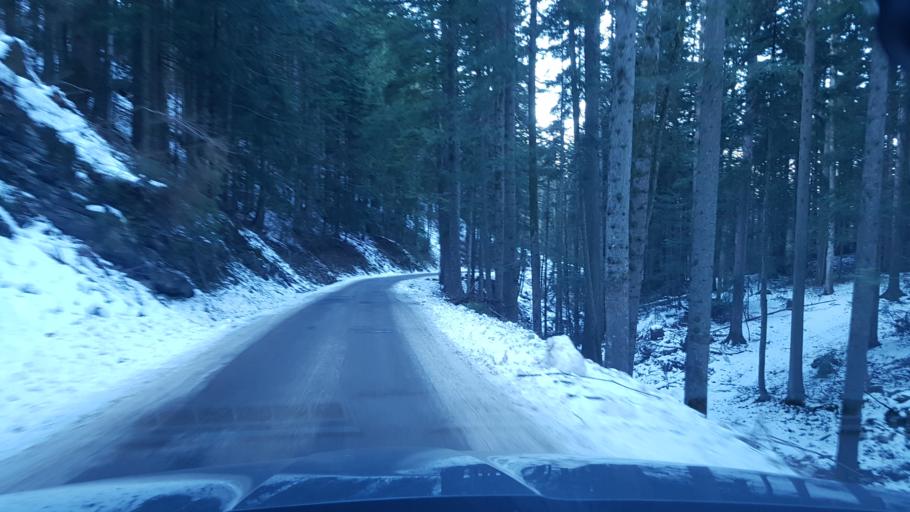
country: AT
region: Salzburg
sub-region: Politischer Bezirk Hallein
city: Scheffau am Tennengebirge
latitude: 47.6308
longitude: 13.2109
